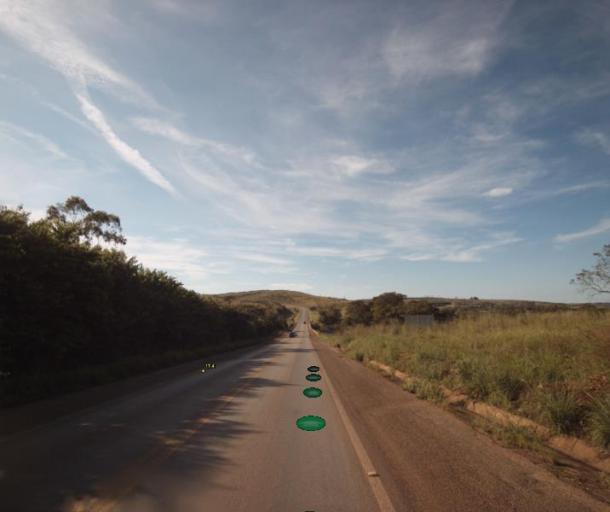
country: BR
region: Federal District
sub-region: Brasilia
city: Brasilia
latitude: -15.7478
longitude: -48.3525
